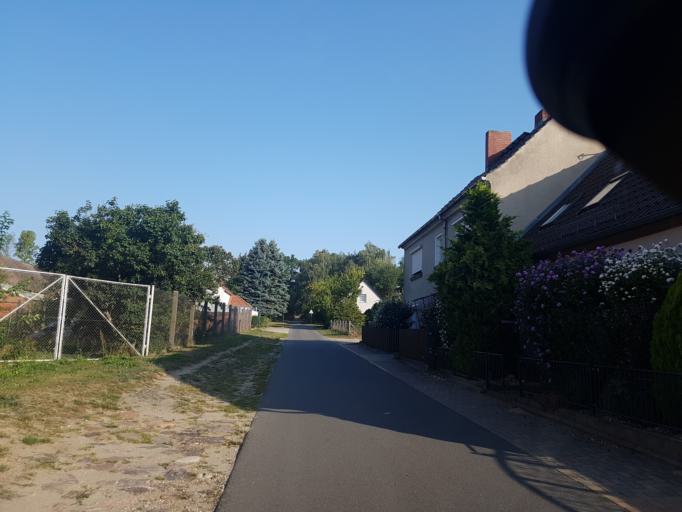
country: DE
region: Saxony-Anhalt
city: Kropstadt
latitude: 51.9691
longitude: 12.7437
